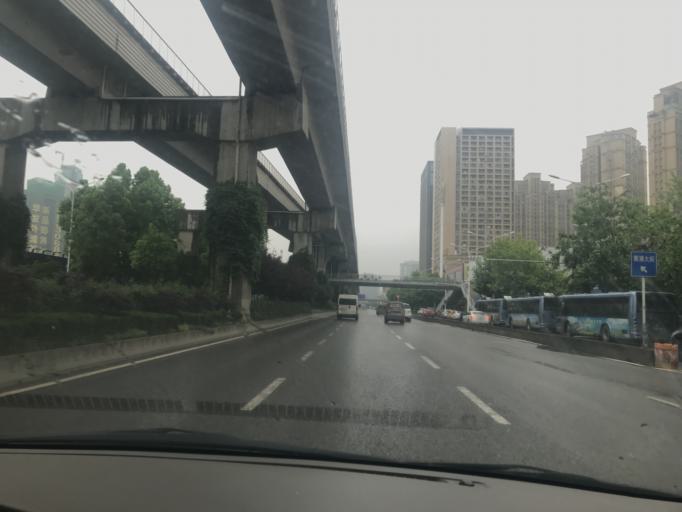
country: CN
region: Hubei
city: Jiang'an
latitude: 30.6266
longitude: 114.3126
